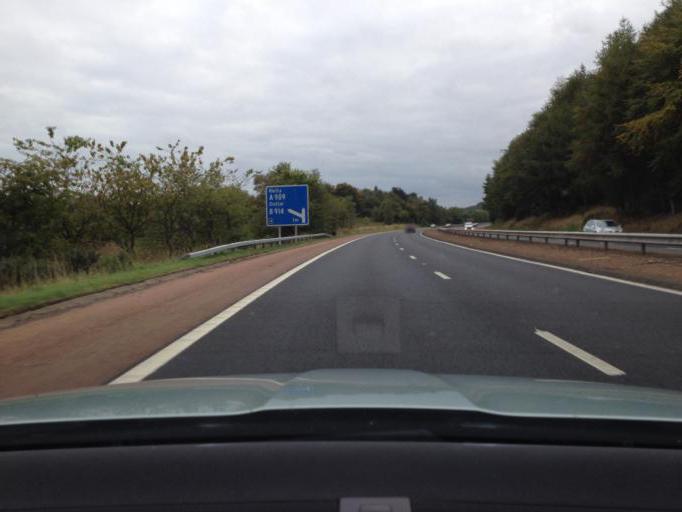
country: GB
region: Scotland
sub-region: Fife
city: Kelty
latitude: 56.1478
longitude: -3.3928
